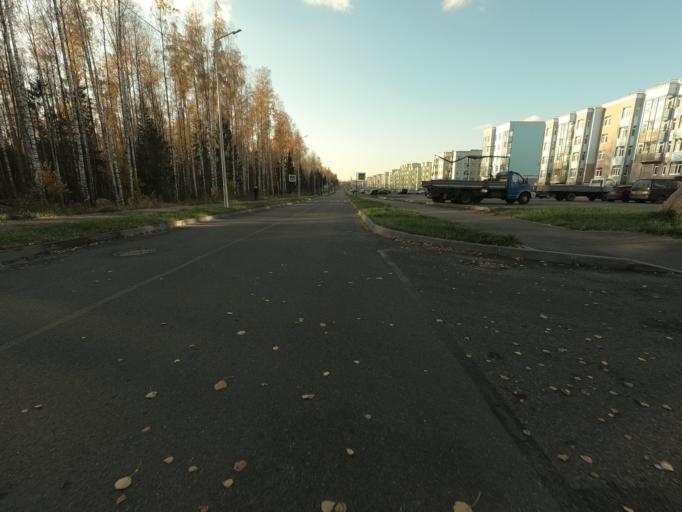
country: RU
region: Leningrad
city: Sertolovo
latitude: 60.1618
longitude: 30.1972
